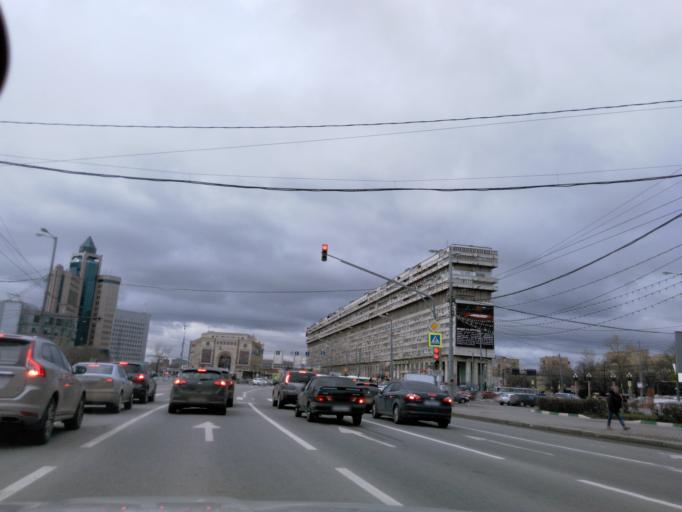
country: RU
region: Moscow
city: Zamoskvorech'ye
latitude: 55.7126
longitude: 37.6224
